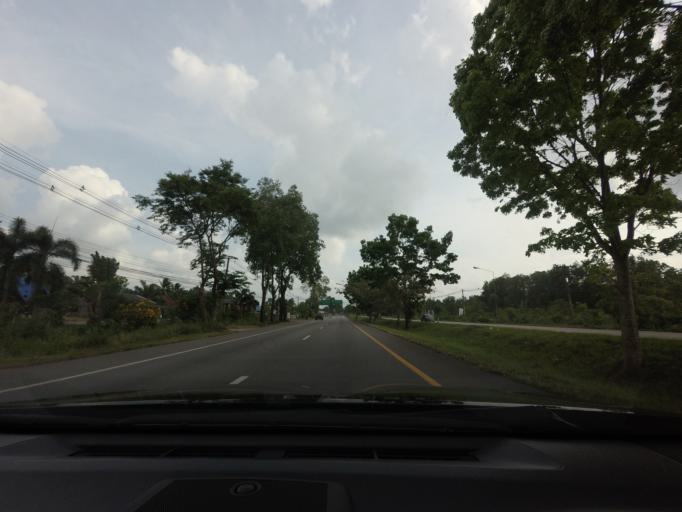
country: TH
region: Chumphon
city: Sawi
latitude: 10.1738
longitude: 99.0963
